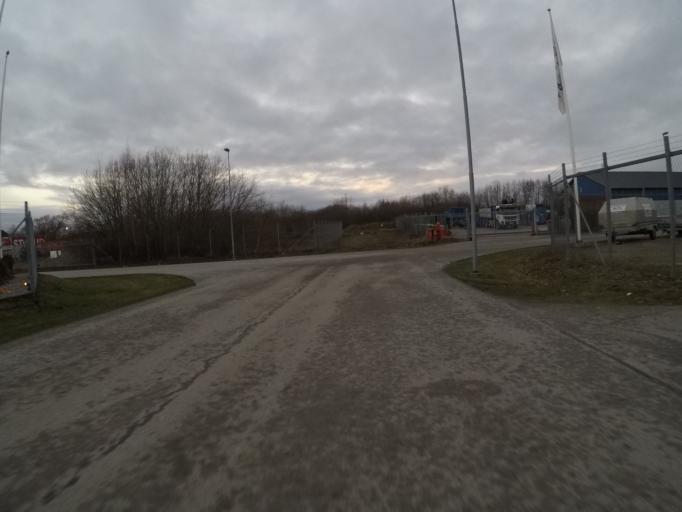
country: SE
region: Skane
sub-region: Sjobo Kommun
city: Sjoebo
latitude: 55.6376
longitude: 13.6897
